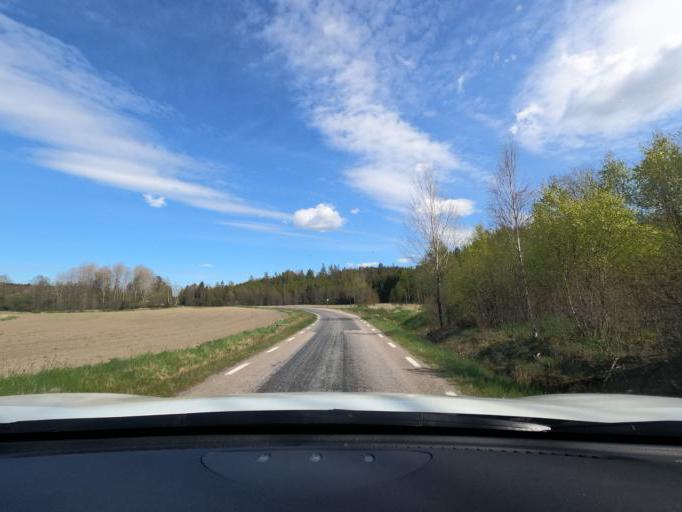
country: SE
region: Vaestra Goetaland
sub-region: Marks Kommun
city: Horred
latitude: 57.4498
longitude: 12.4594
